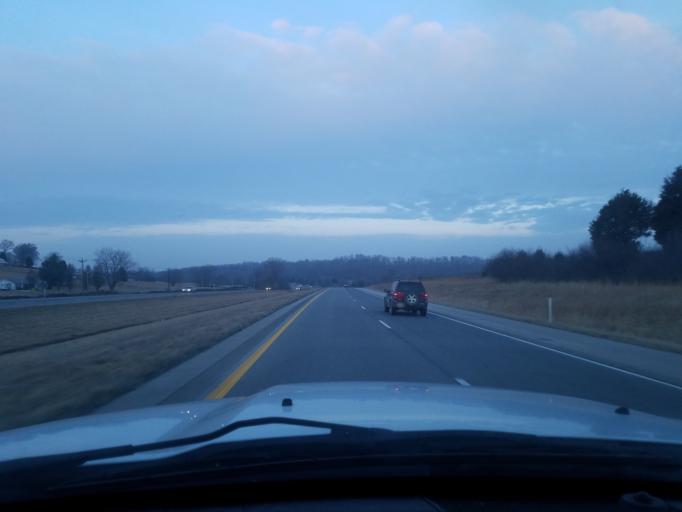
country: US
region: Indiana
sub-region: Harrison County
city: Corydon
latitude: 38.2419
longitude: -86.1958
